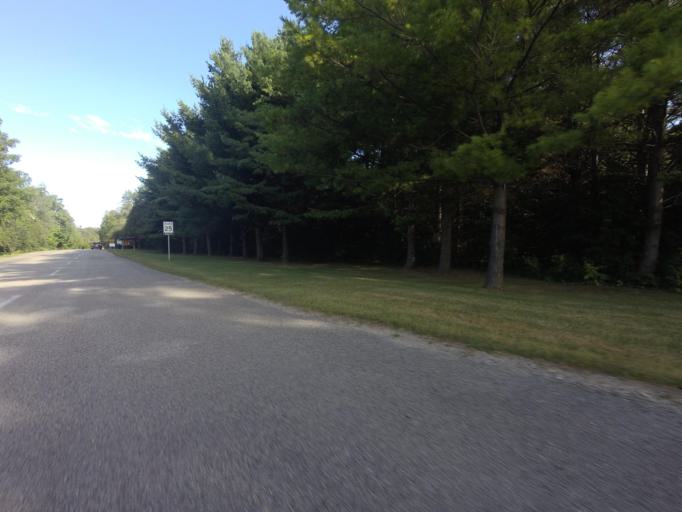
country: CA
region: Ontario
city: Waterloo
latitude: 43.6698
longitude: -80.4419
